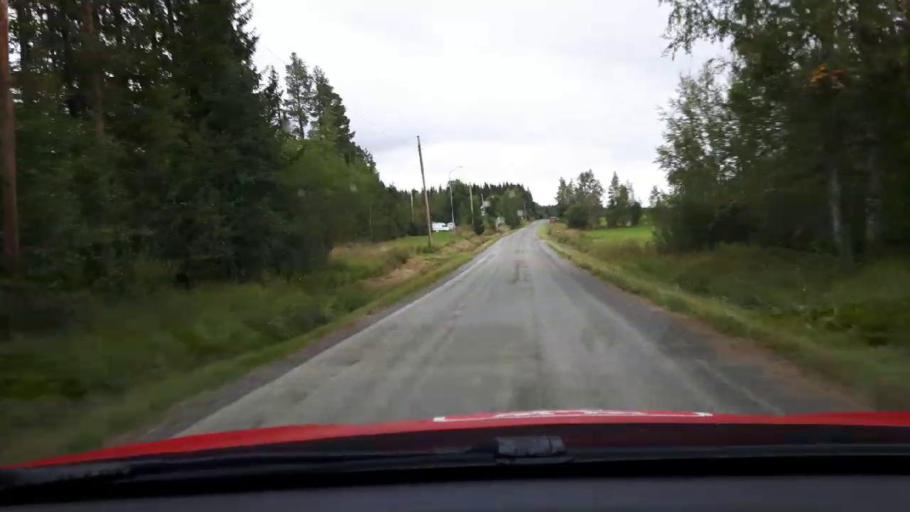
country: SE
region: Jaemtland
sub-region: Bergs Kommun
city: Hoverberg
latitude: 62.8664
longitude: 14.2984
